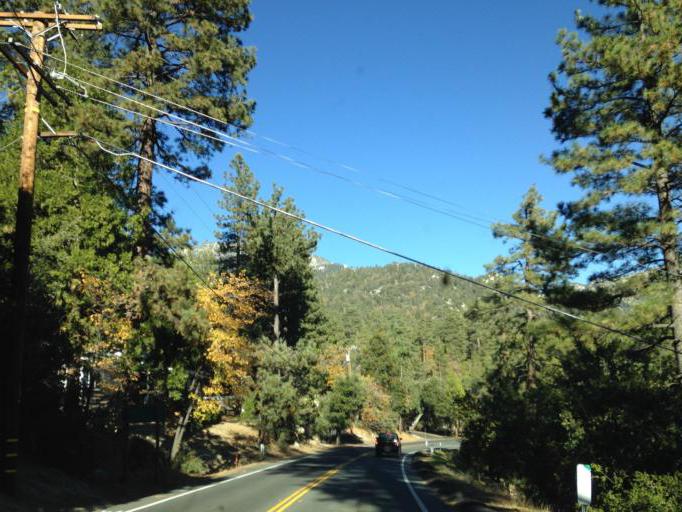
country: US
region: California
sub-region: Riverside County
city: Idyllwild-Pine Cove
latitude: 33.7527
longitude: -116.7259
